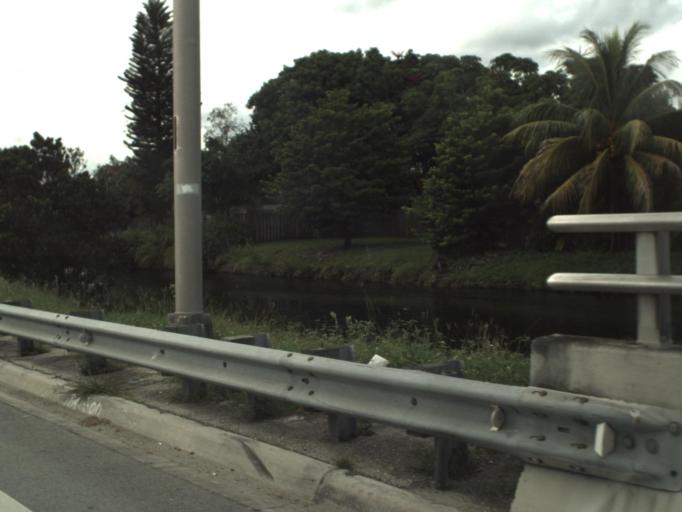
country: US
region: Florida
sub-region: Miami-Dade County
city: Westchester
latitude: 25.7621
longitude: -80.3376
